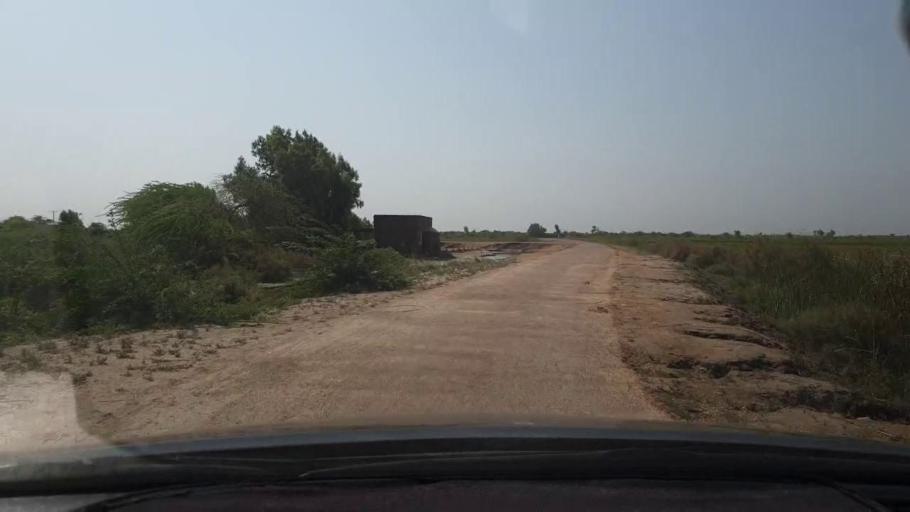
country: PK
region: Sindh
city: Tando Bago
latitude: 24.7032
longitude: 69.1072
